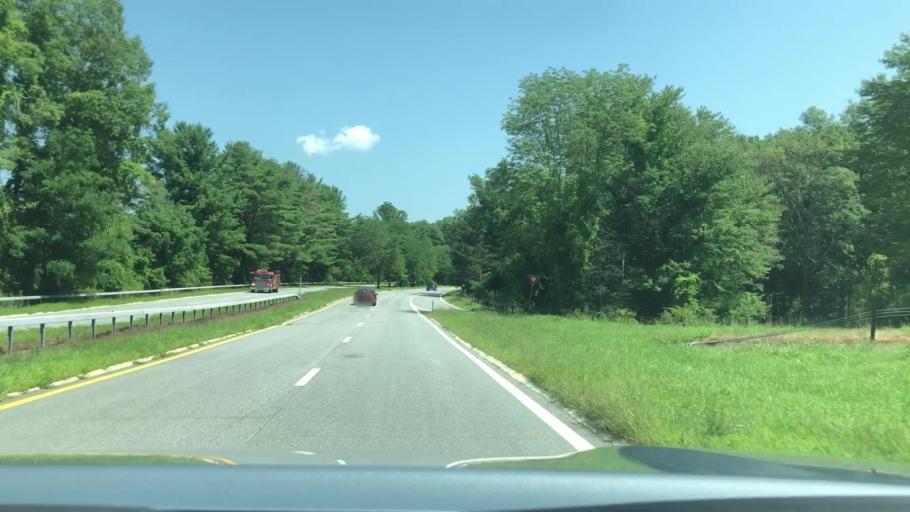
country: US
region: New York
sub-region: Orange County
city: Fort Montgomery
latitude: 41.3097
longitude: -74.0240
